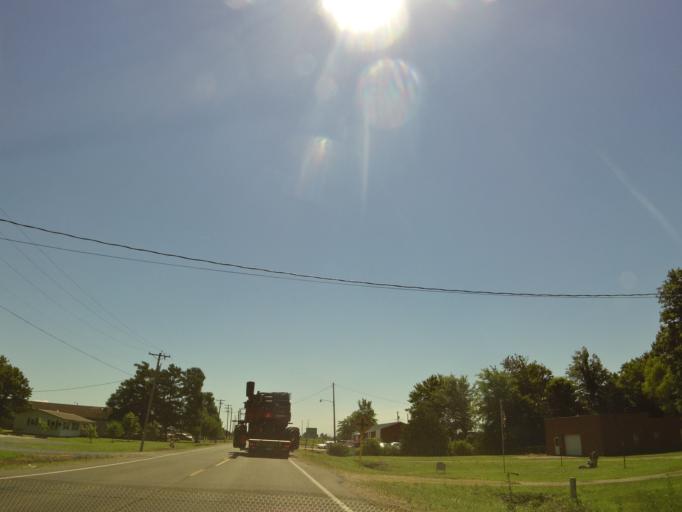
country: US
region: Missouri
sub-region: New Madrid County
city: Gideon
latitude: 36.5536
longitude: -89.8122
